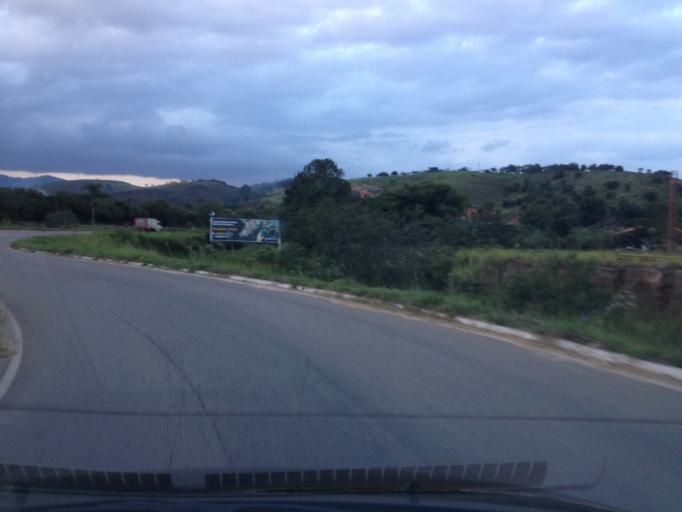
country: BR
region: Minas Gerais
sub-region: Sao Lourenco
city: Sao Lourenco
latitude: -22.0851
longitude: -45.0369
